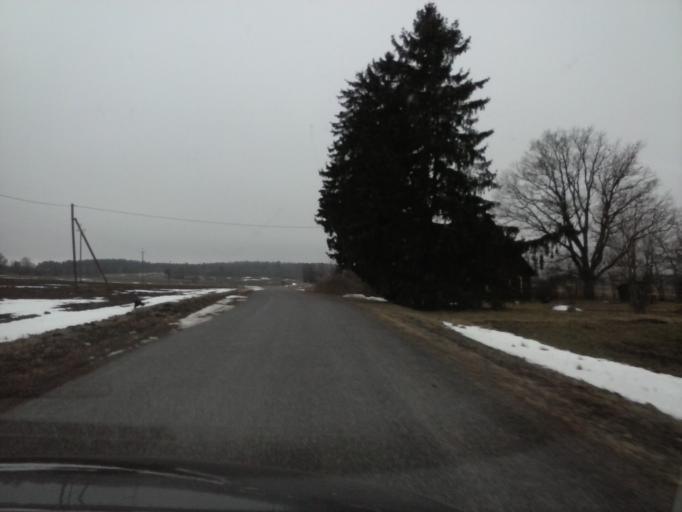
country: EE
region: Vorumaa
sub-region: Antsla vald
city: Vana-Antsla
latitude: 57.6112
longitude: 26.3588
